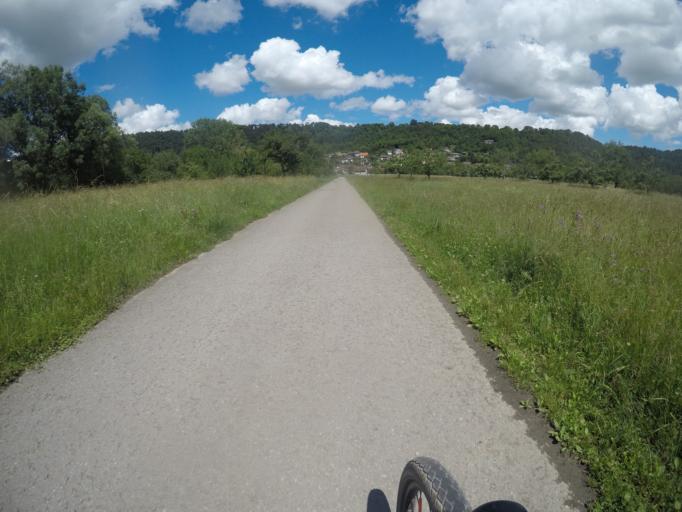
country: DE
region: Baden-Wuerttemberg
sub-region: Tuebingen Region
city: Haigerloch
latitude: 48.4446
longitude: 8.8062
